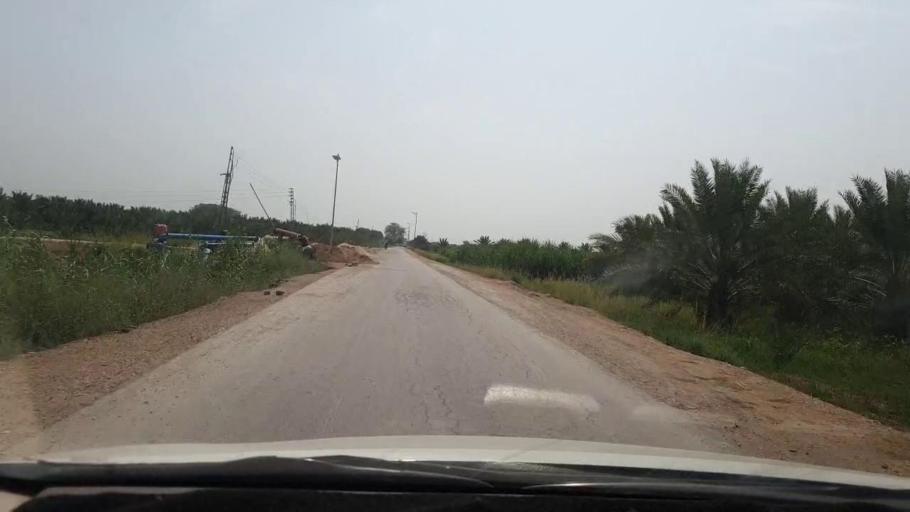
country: PK
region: Sindh
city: Rohri
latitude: 27.5384
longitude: 69.0246
